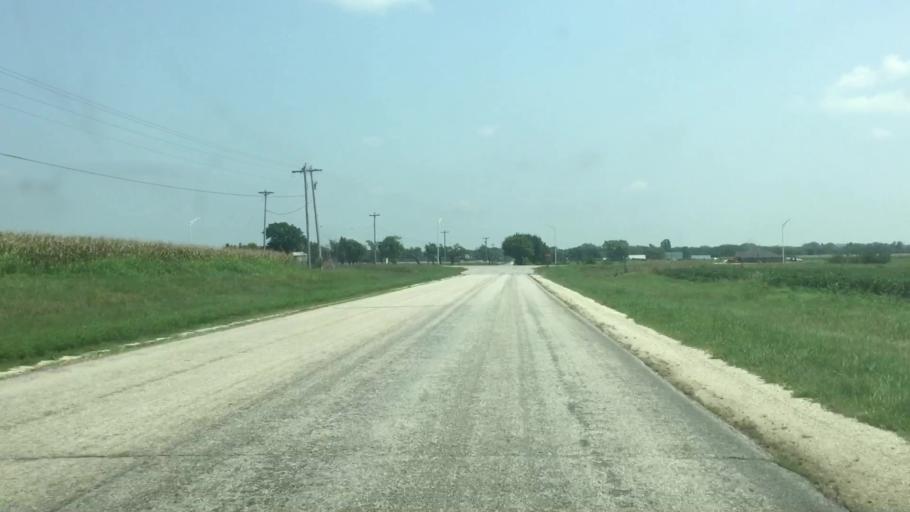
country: US
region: Kansas
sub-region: Allen County
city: Iola
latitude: 37.9512
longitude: -95.3833
